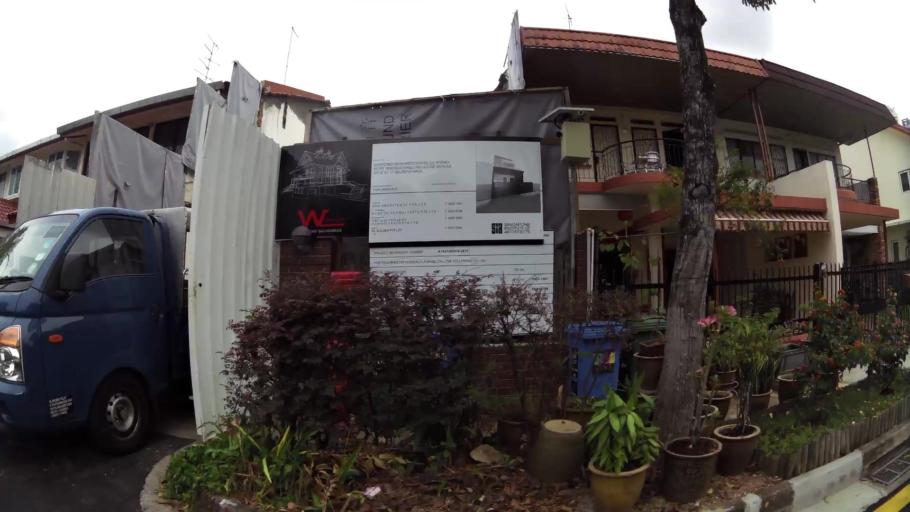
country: SG
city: Singapore
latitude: 1.3132
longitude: 103.7849
